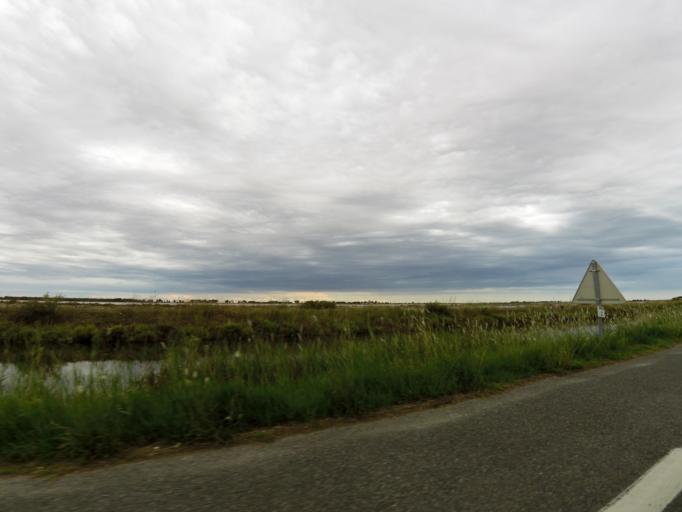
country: FR
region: Languedoc-Roussillon
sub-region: Departement du Gard
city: Le Grau-du-Roi
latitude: 43.5341
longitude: 4.1468
